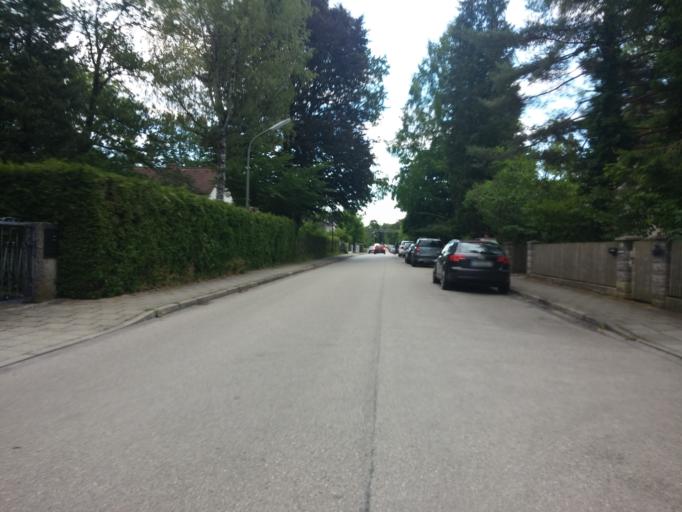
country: DE
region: Bavaria
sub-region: Upper Bavaria
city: Haar
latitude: 48.1079
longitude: 11.7442
